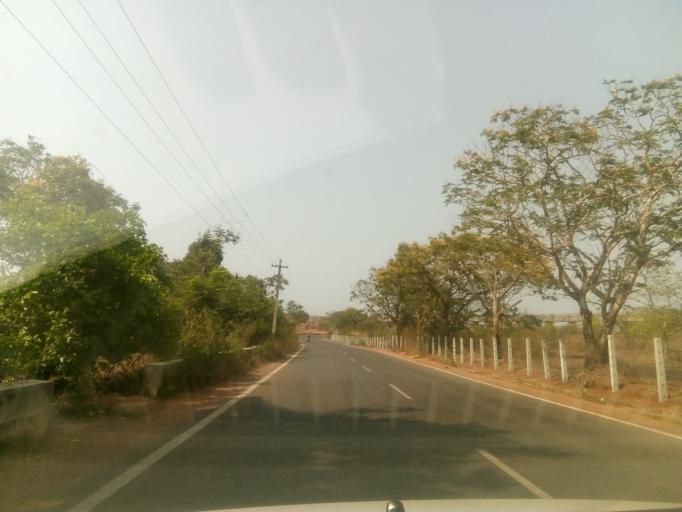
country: IN
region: Goa
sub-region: North Goa
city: Colovale
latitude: 15.6849
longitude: 73.8374
